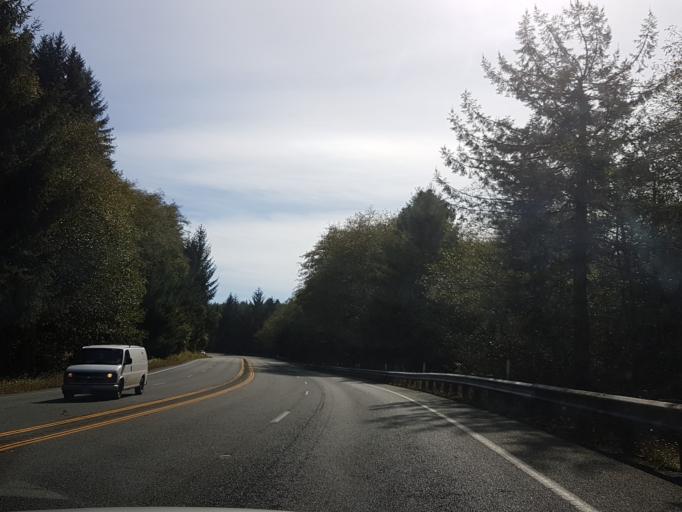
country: US
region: California
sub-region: Del Norte County
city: Bertsch-Oceanview
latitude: 41.4863
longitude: -124.0509
